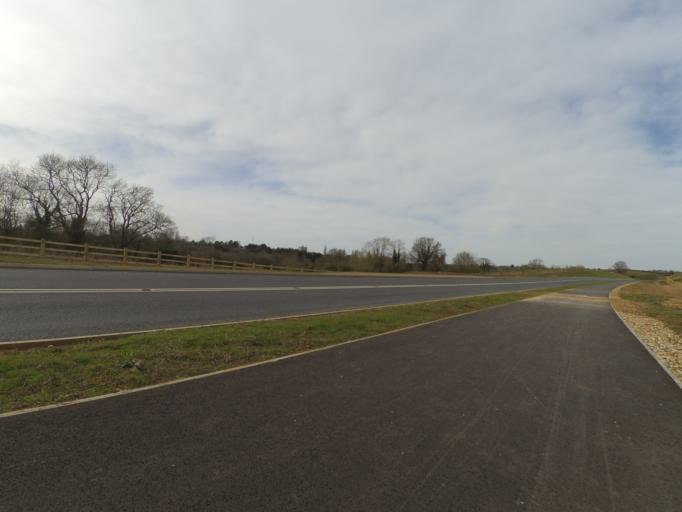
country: GB
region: England
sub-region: Warwickshire
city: Rugby
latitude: 52.3717
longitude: -1.2244
